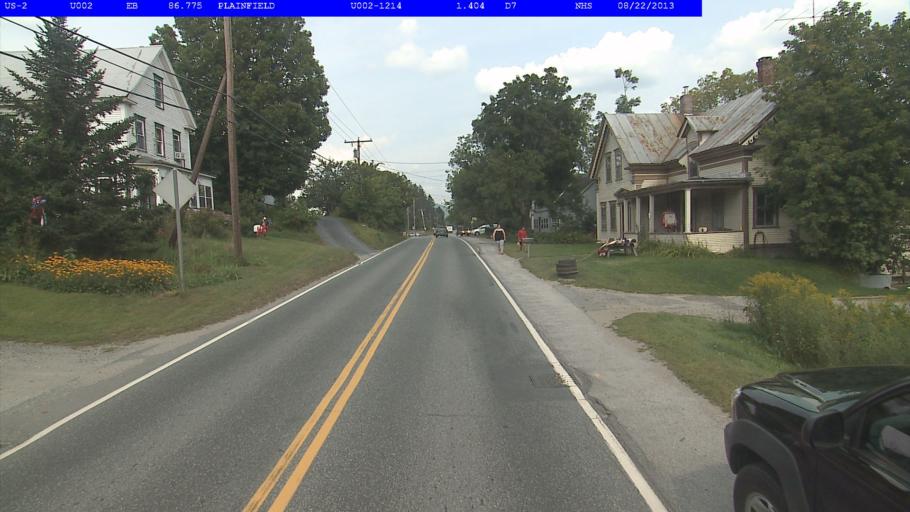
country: US
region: Vermont
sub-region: Washington County
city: Barre
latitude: 44.2790
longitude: -72.4235
